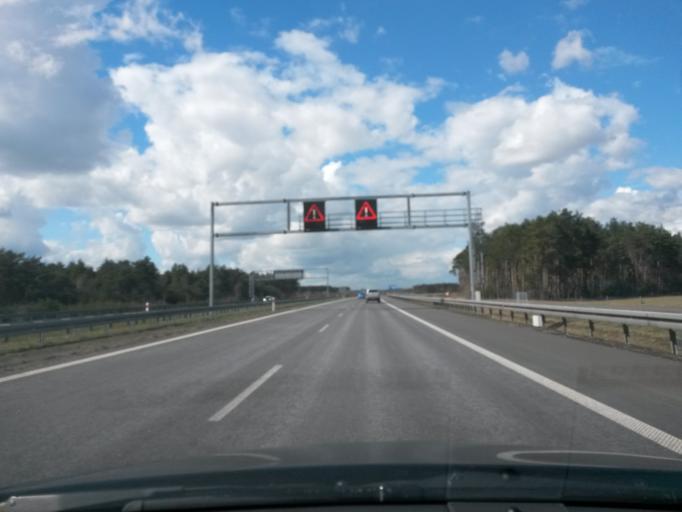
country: PL
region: Greater Poland Voivodeship
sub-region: Powiat kolski
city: Dabie
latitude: 52.0799
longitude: 18.7996
